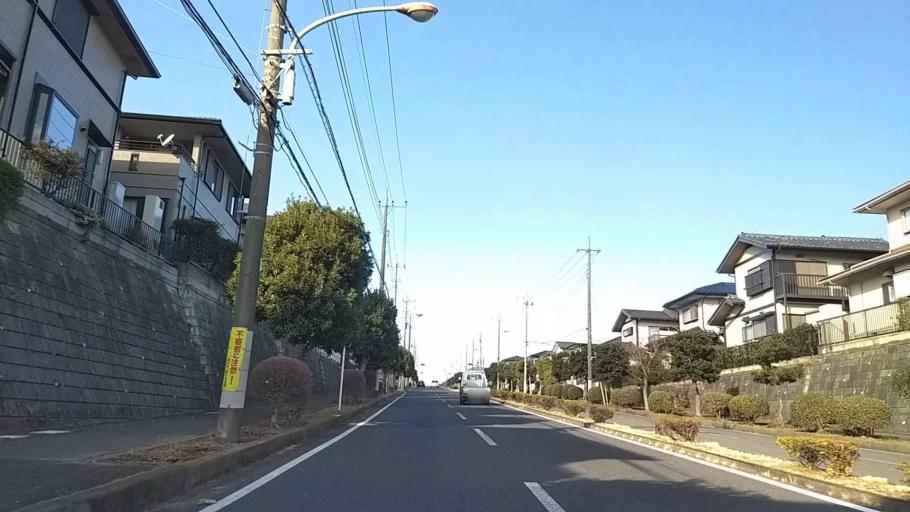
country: JP
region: Kanagawa
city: Atsugi
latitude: 35.4355
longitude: 139.3306
